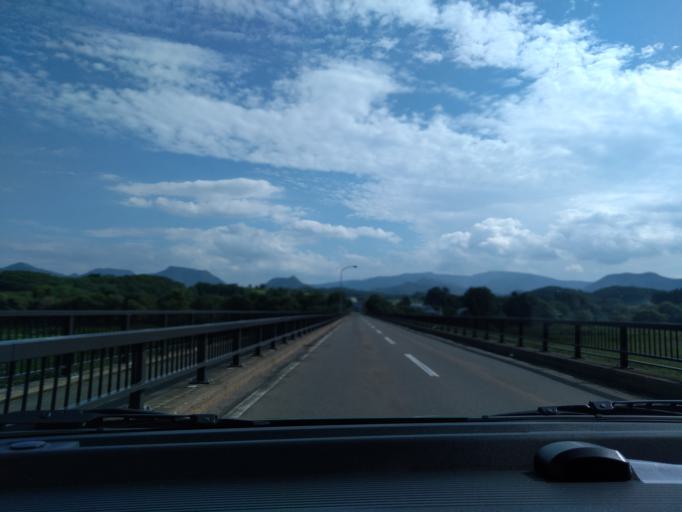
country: JP
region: Iwate
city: Shizukuishi
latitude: 39.6678
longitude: 140.9817
